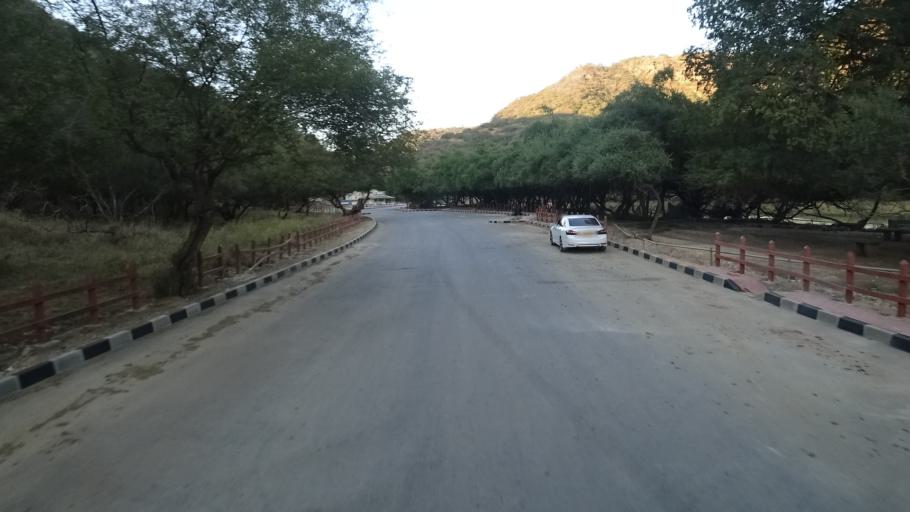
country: OM
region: Zufar
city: Salalah
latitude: 17.1029
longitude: 54.4519
